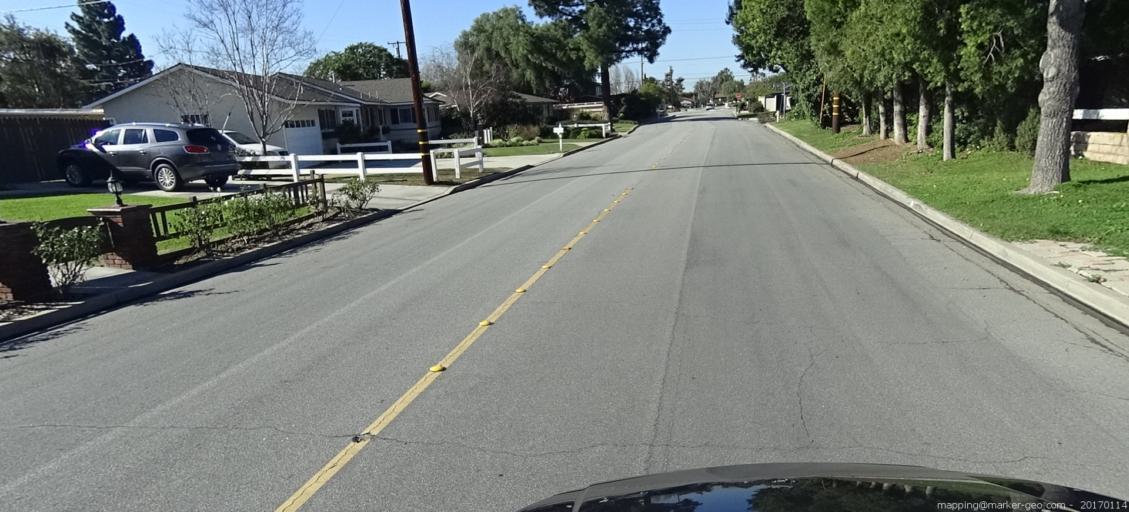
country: US
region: California
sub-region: Orange County
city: North Tustin
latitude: 33.7631
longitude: -117.8044
